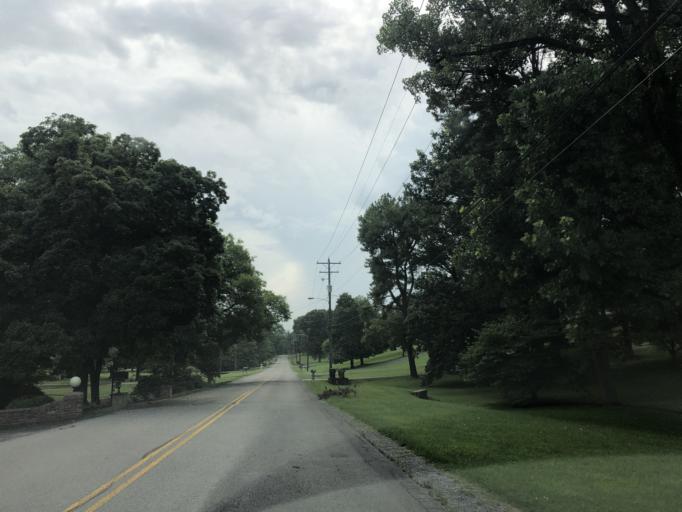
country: US
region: Tennessee
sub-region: Davidson County
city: Lakewood
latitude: 36.1826
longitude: -86.6846
